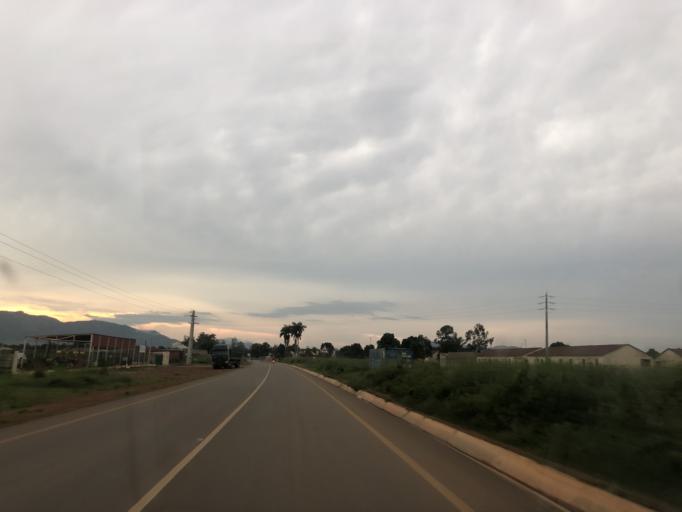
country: AO
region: Cuanza Sul
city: Uacu Cungo
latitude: -11.3511
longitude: 15.1098
